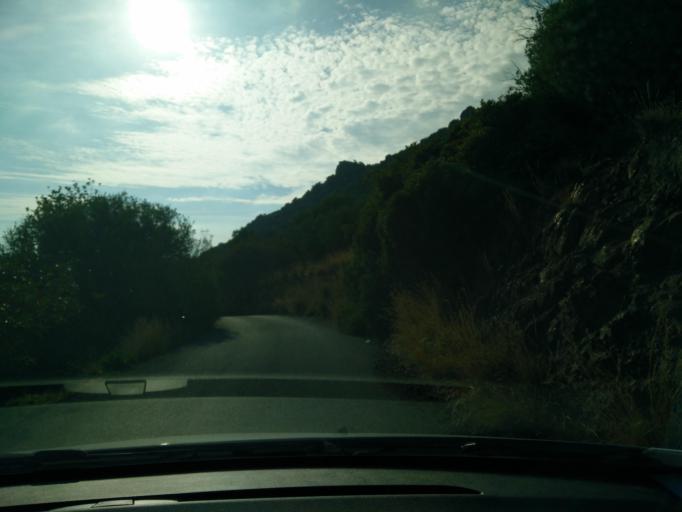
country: GR
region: Crete
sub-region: Nomos Lasithiou
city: Gra Liyia
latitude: 35.0259
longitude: 25.5617
